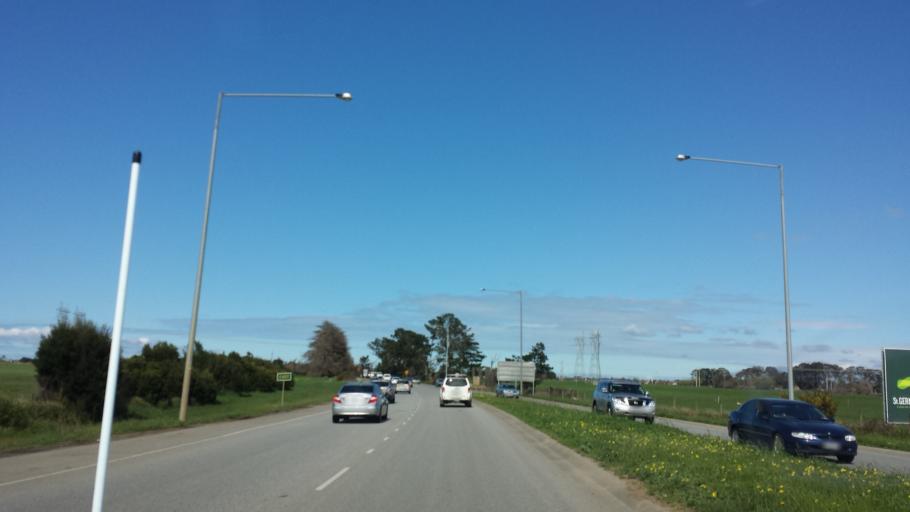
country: AU
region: Victoria
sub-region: Casey
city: Cranbourne East
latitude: -38.0899
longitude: 145.3328
